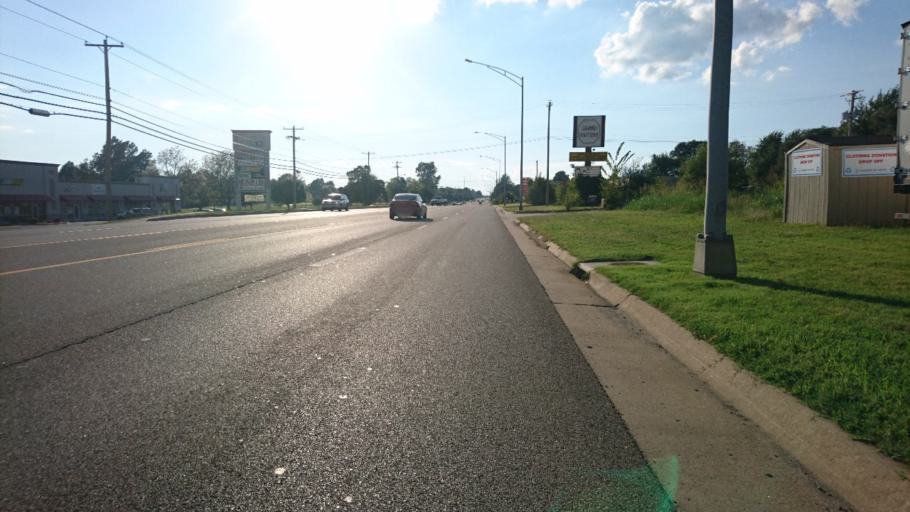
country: US
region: Missouri
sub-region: Greene County
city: Springfield
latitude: 37.2124
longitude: -93.3563
